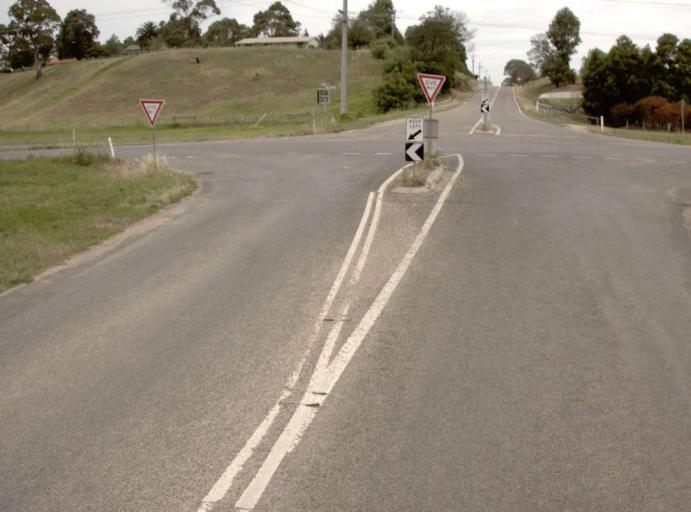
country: AU
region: Victoria
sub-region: East Gippsland
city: Bairnsdale
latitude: -37.7978
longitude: 147.4400
